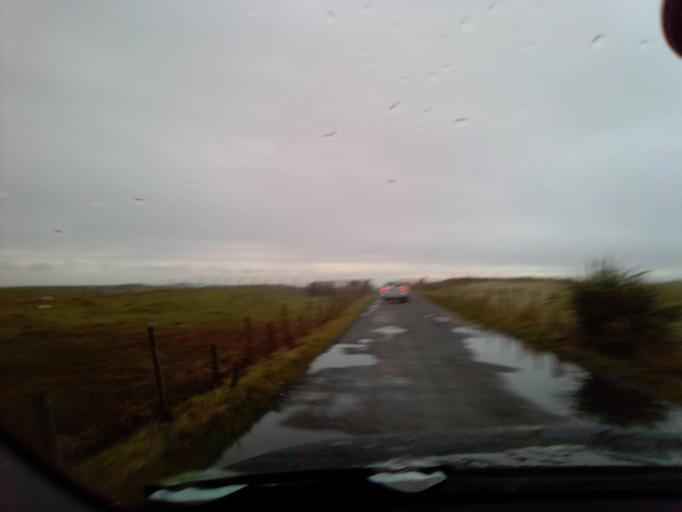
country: IE
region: Ulster
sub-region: County Donegal
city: Ramelton
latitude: 55.2585
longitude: -7.6806
